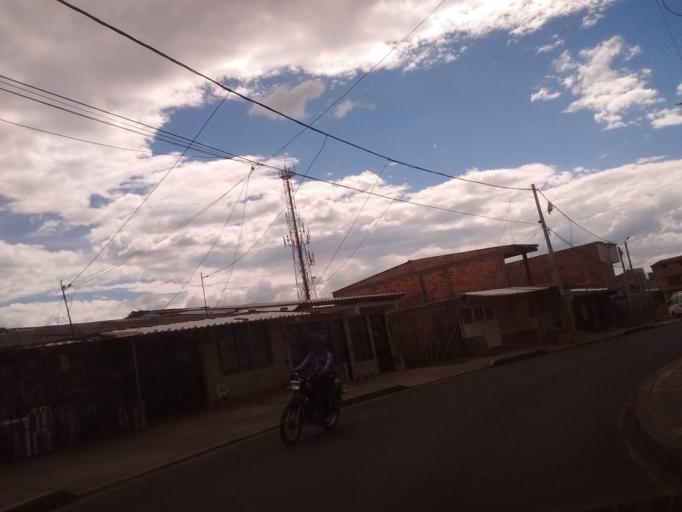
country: CO
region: Cauca
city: Popayan
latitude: 2.4724
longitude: -76.5559
